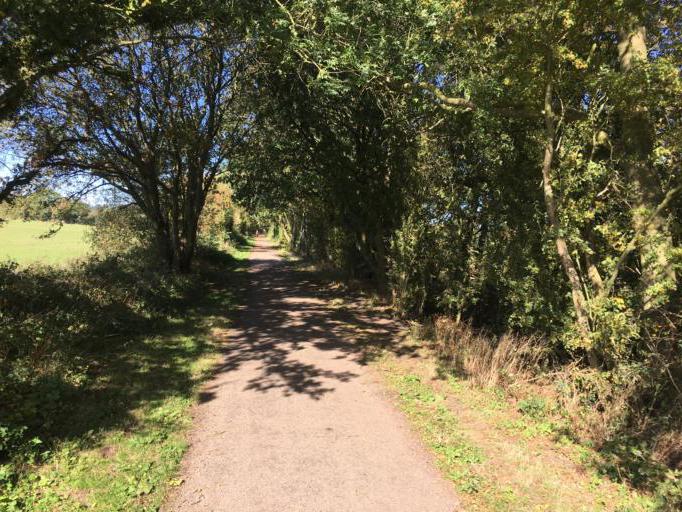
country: GB
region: England
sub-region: Warwickshire
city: Kenilworth
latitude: 52.3701
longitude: -1.5893
